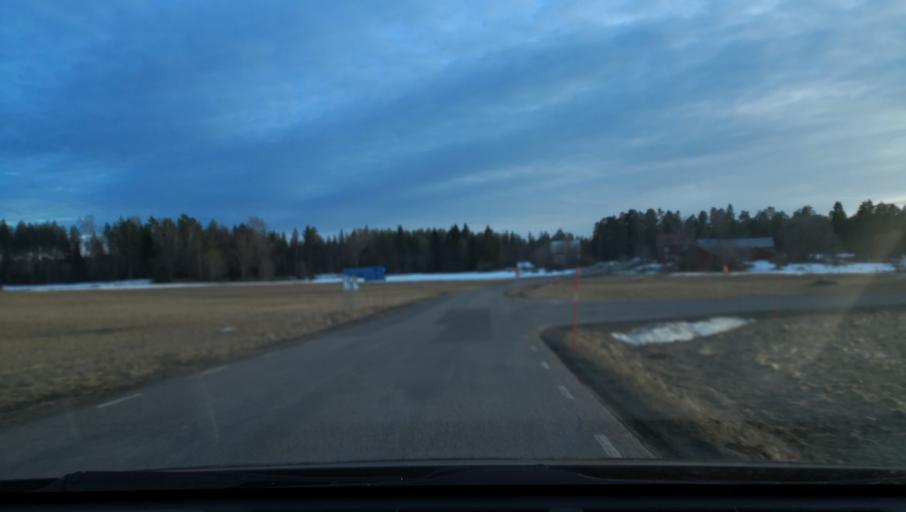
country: SE
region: Uppsala
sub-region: Osthammars Kommun
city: Osterbybruk
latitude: 60.2382
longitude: 17.9235
